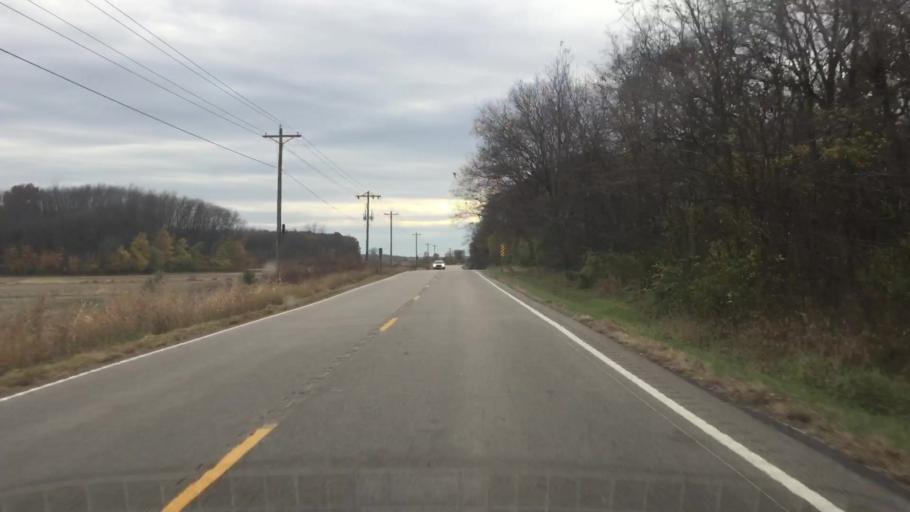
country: US
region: Missouri
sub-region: Callaway County
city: Holts Summit
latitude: 38.5988
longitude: -92.0043
